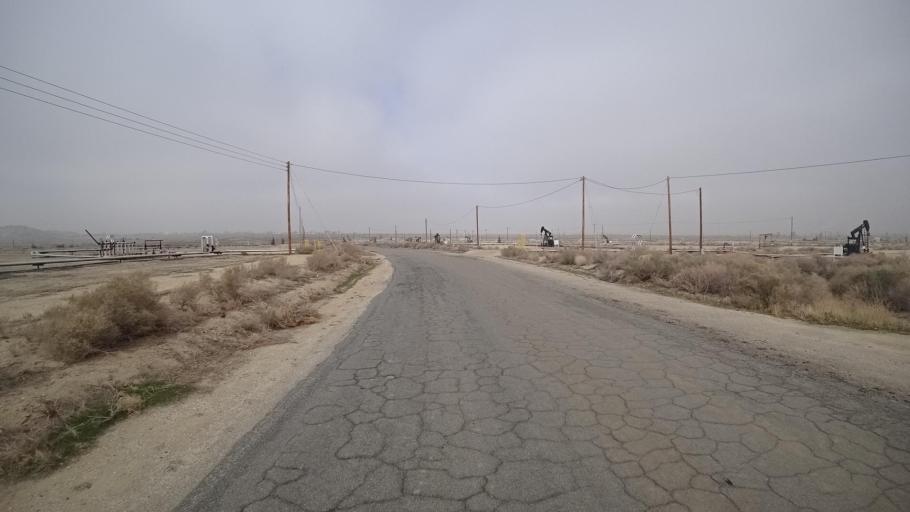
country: US
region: California
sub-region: Kern County
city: Maricopa
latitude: 35.0416
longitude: -119.3848
